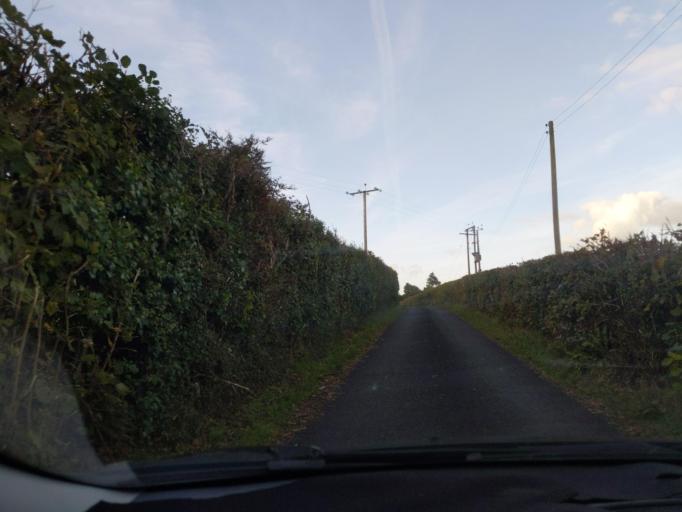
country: GB
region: England
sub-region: Devon
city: Bovey Tracey
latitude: 50.6327
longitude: -3.6451
